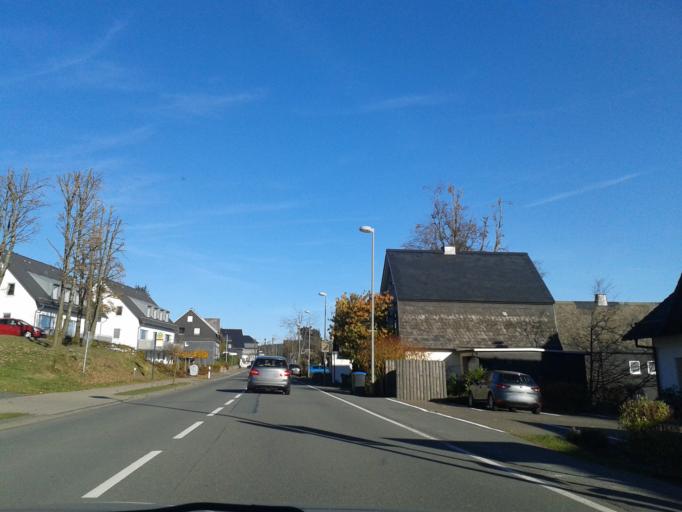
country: DE
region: North Rhine-Westphalia
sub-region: Regierungsbezirk Arnsberg
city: Winterberg
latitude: 51.1637
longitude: 8.4829
